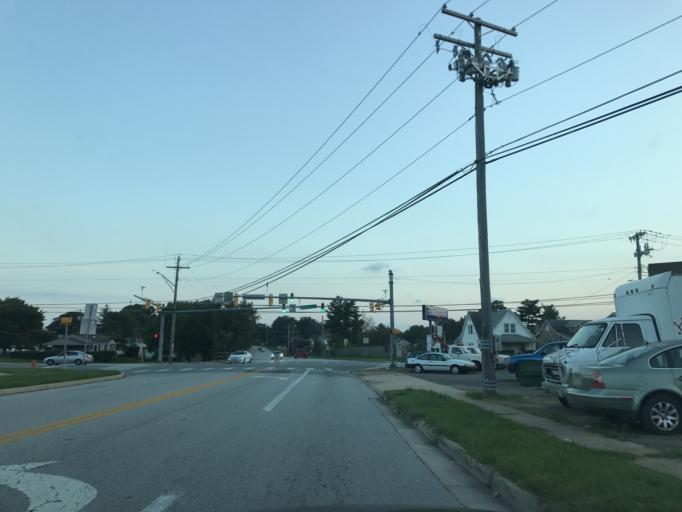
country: US
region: Maryland
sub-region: Baltimore County
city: Dundalk
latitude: 39.2735
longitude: -76.5178
